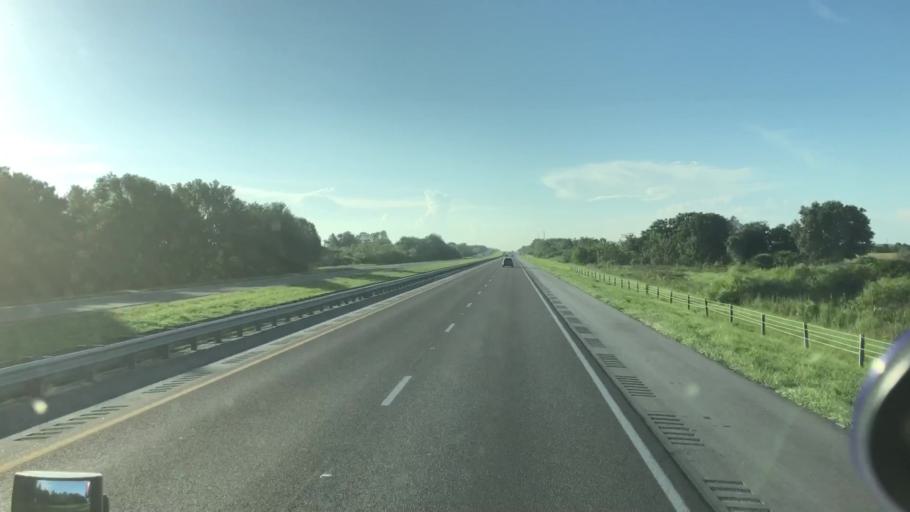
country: US
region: Florida
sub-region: Osceola County
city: Saint Cloud
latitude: 28.0476
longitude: -81.2155
